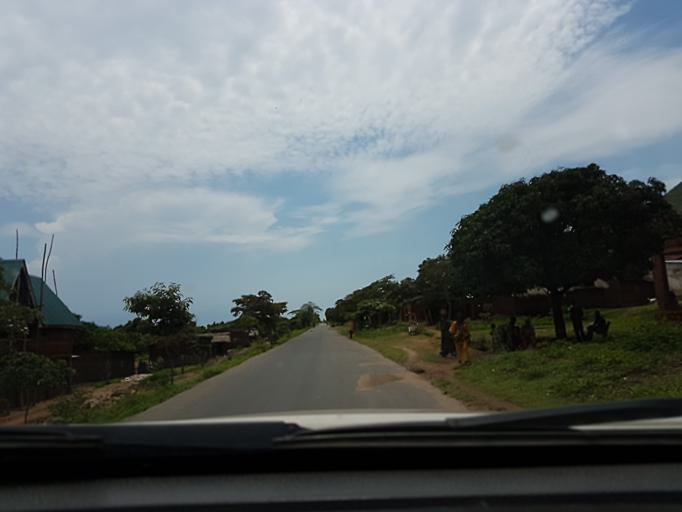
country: CD
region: South Kivu
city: Uvira
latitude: -3.2450
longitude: 29.1612
